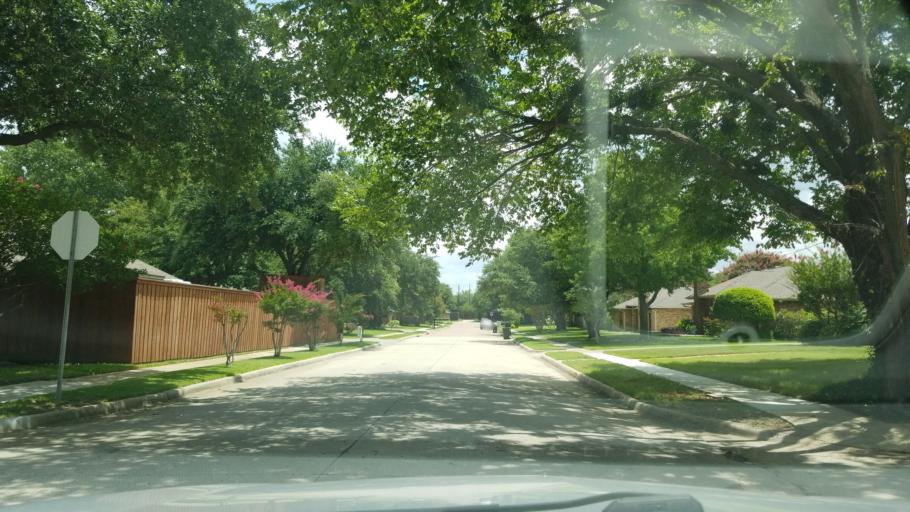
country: US
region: Texas
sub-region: Dallas County
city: Coppell
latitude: 32.9700
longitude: -96.9680
